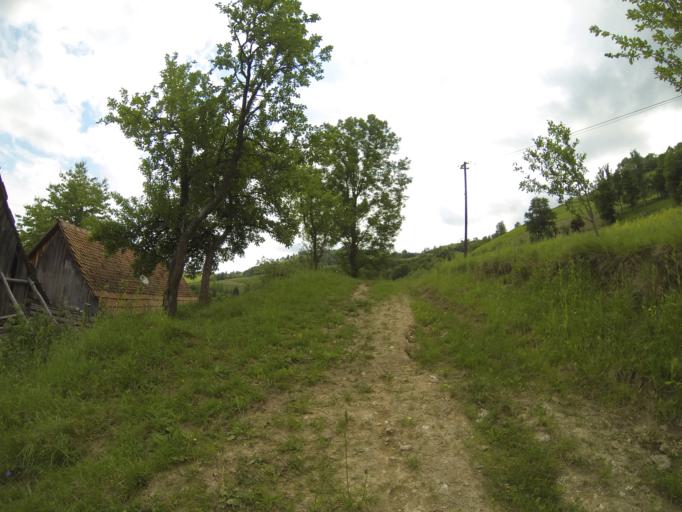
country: RO
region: Brasov
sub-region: Comuna Poiana Marului
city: Poiana Marului
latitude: 45.6468
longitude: 25.2903
